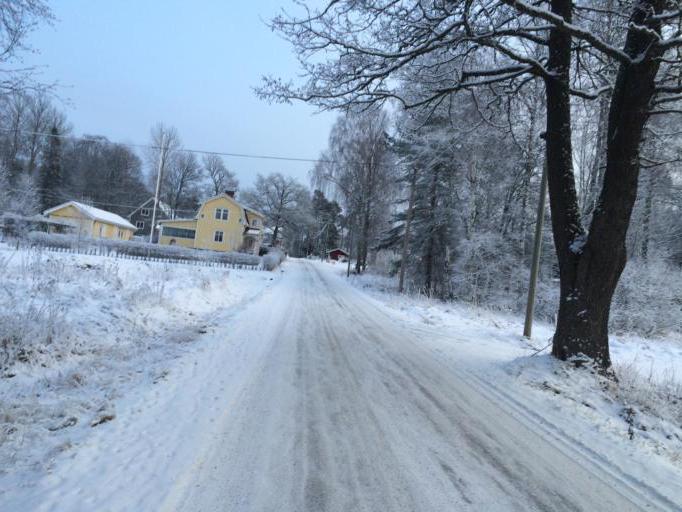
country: SE
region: Uppsala
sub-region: Enkopings Kommun
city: Orsundsbro
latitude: 59.9088
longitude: 17.2088
